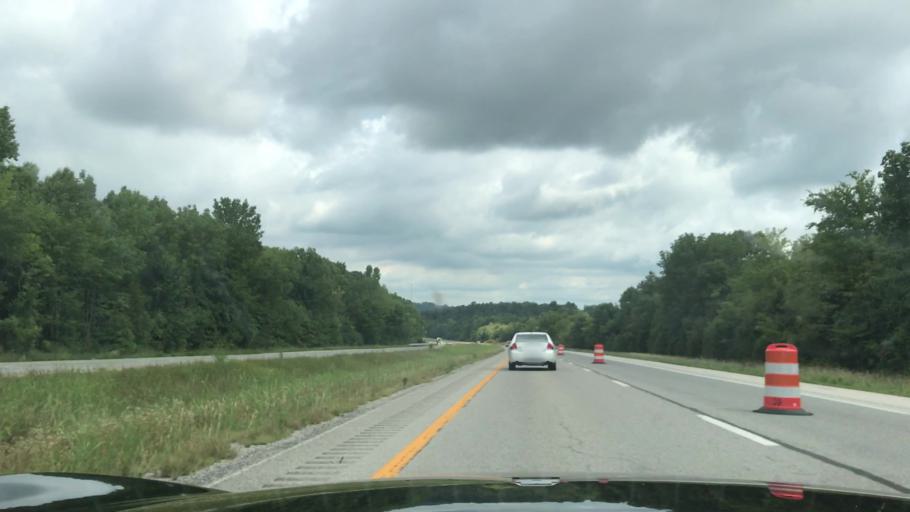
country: US
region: Kentucky
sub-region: Butler County
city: Morgantown
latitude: 37.1160
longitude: -86.6414
